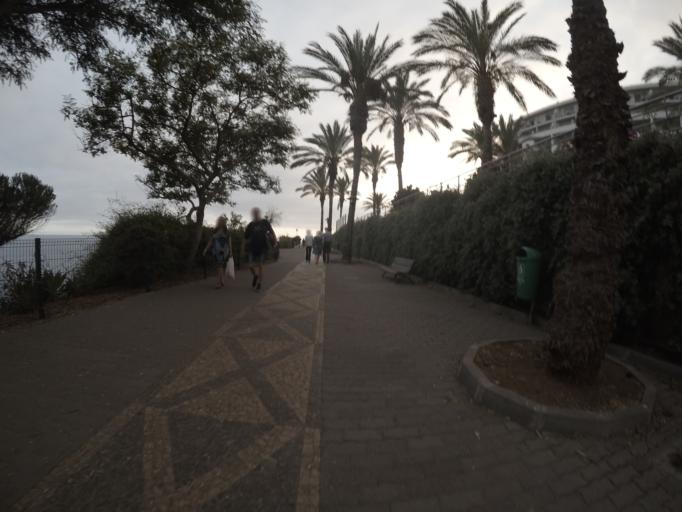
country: PT
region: Madeira
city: Camara de Lobos
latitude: 32.6337
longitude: -16.9446
